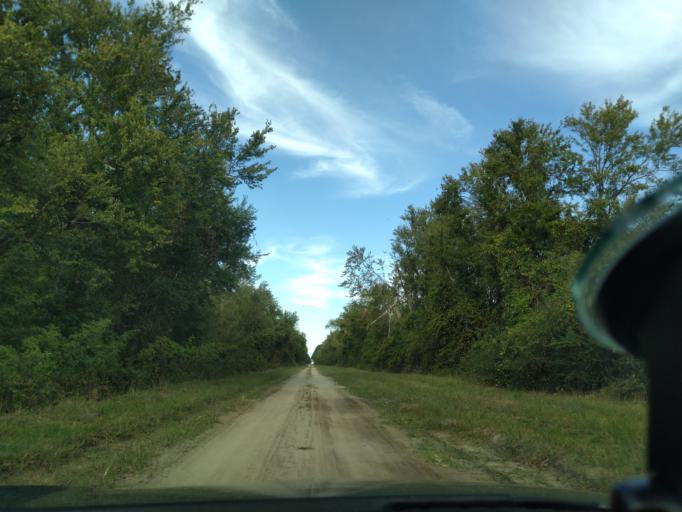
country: US
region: North Carolina
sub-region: Beaufort County
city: Belhaven
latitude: 35.7184
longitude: -76.5808
